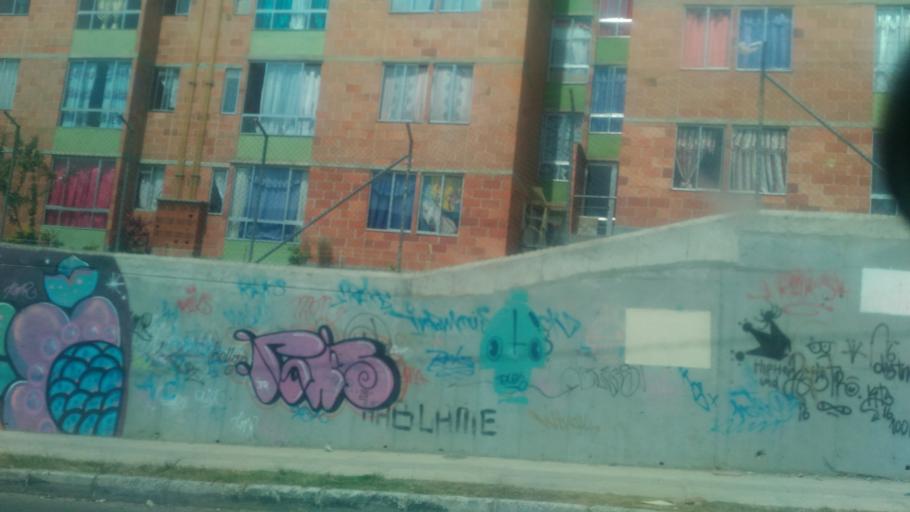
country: CO
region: Antioquia
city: Medellin
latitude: 6.2958
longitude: -75.5867
